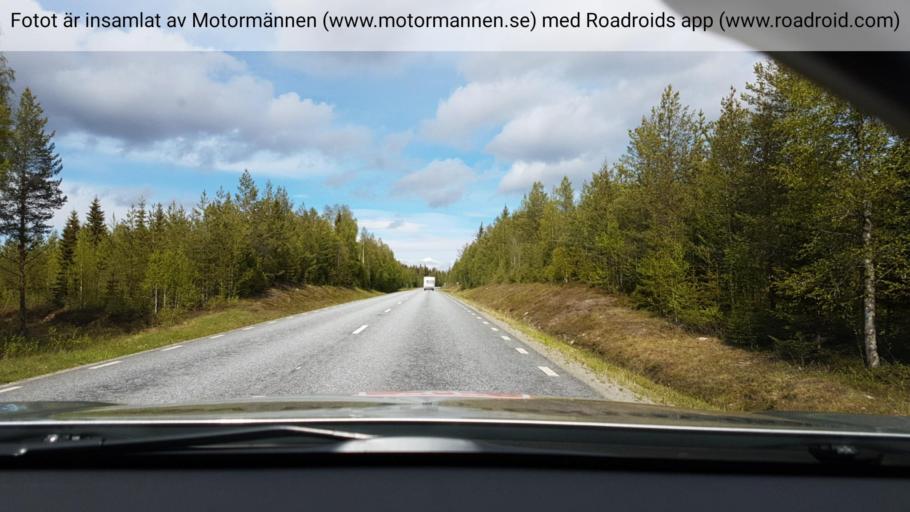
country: SE
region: Vaesterbotten
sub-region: Asele Kommun
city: Asele
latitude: 64.1935
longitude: 17.4888
